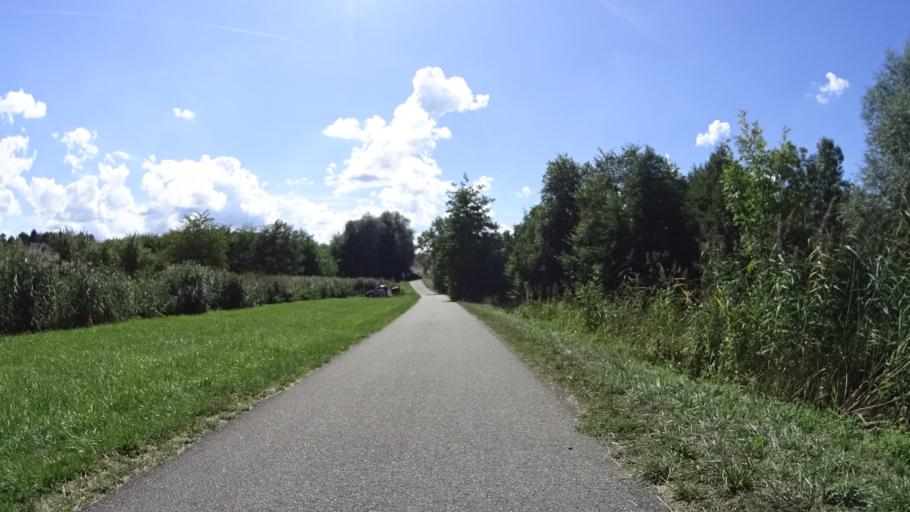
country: FR
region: Alsace
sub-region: Departement du Haut-Rhin
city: Aspach
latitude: 47.6599
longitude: 7.2358
